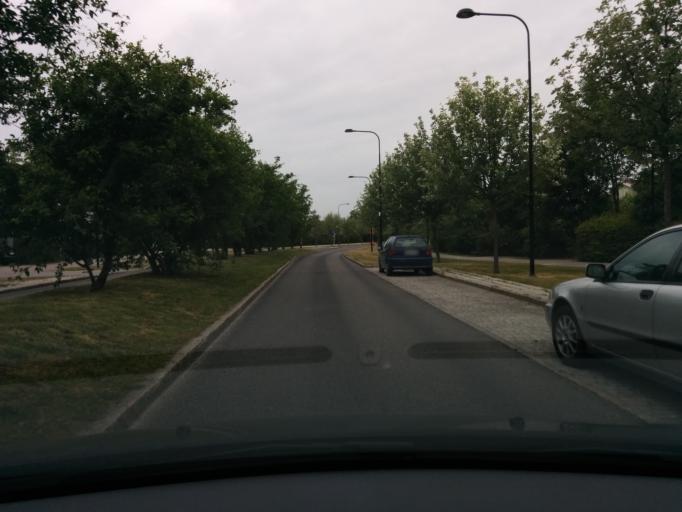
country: SE
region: Stockholm
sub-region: Stockholms Kommun
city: Arsta
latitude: 59.2842
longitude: 18.0697
